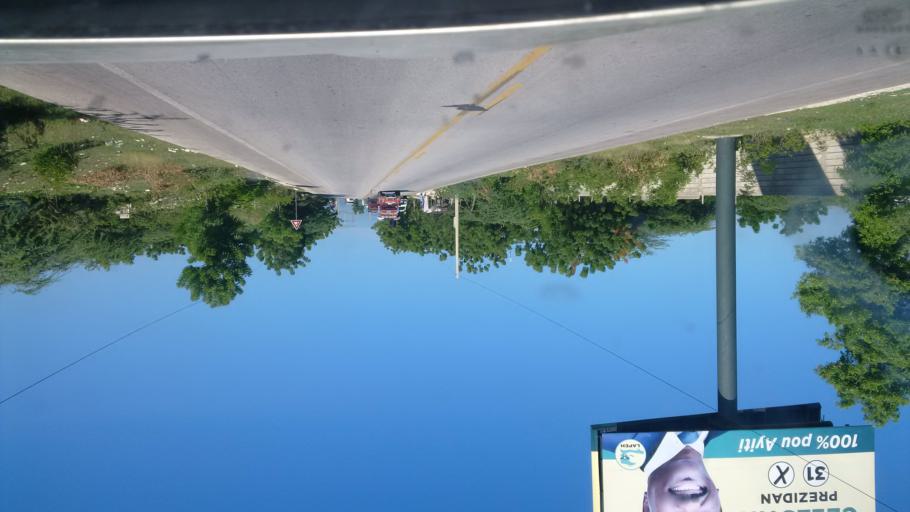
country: HT
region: Ouest
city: Cabaret
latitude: 18.8690
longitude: -72.6080
